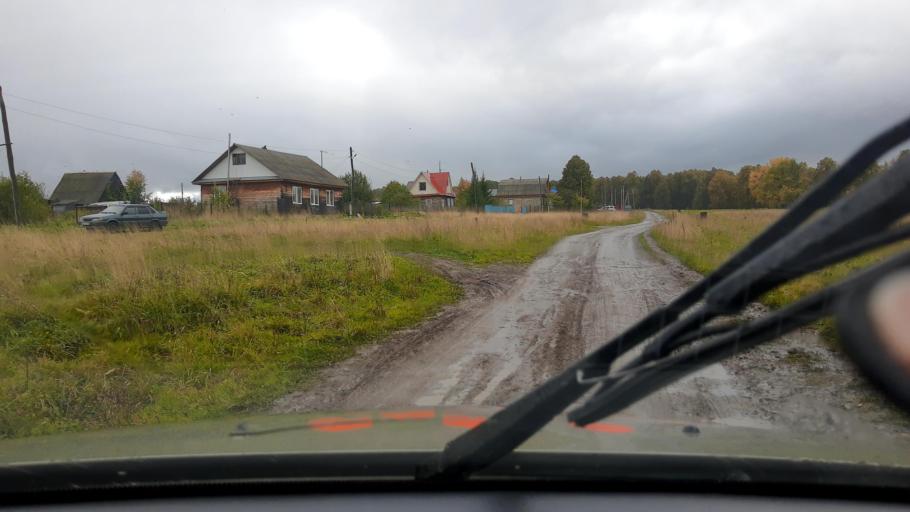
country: RU
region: Bashkortostan
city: Kudeyevskiy
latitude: 54.8765
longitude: 56.6289
